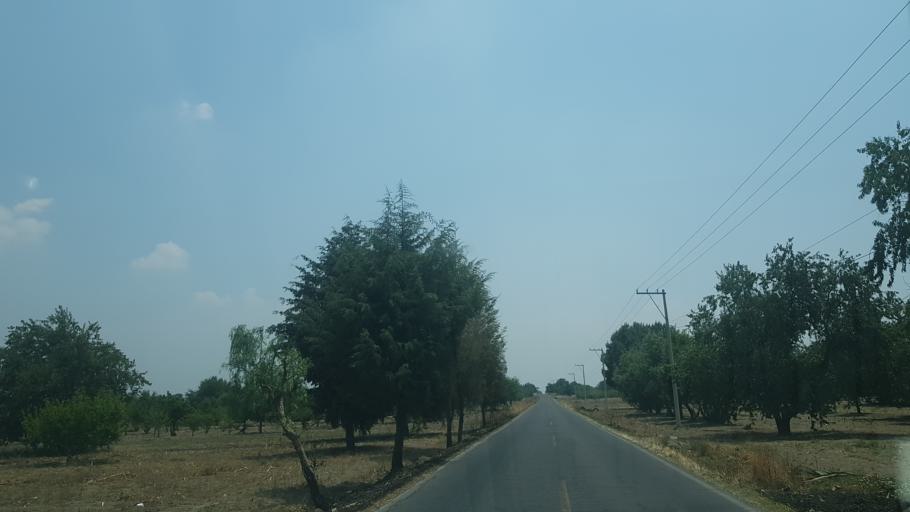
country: MX
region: Puebla
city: San Andres Calpan
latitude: 19.0987
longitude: -98.4273
